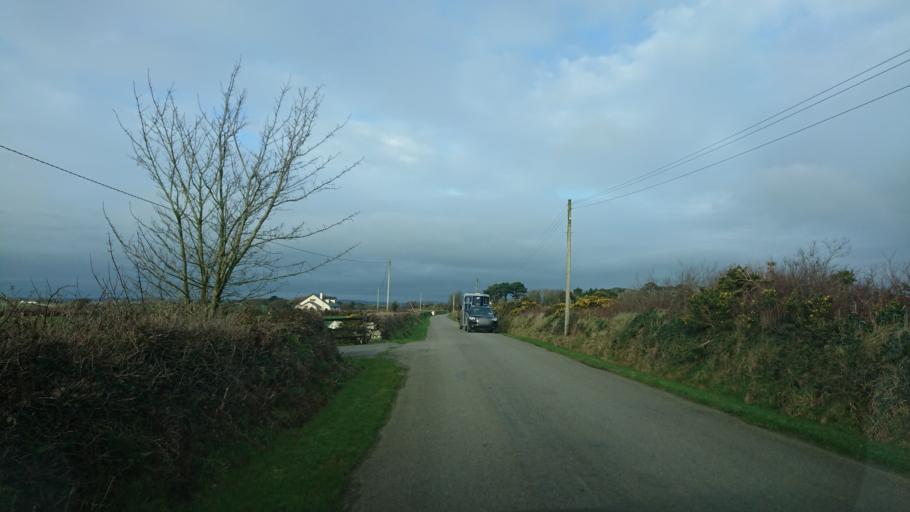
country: IE
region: Munster
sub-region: Waterford
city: Tra Mhor
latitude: 52.1530
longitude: -7.2137
